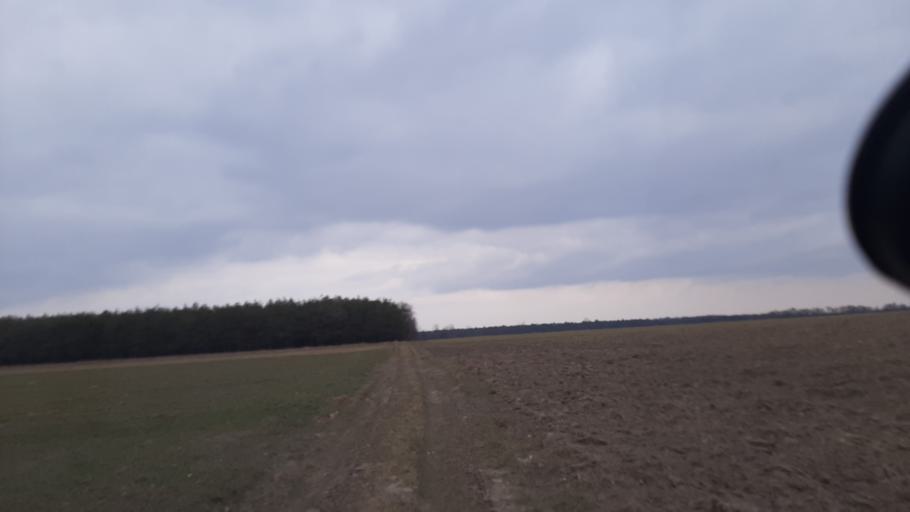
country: PL
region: Lublin Voivodeship
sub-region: Powiat lubelski
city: Garbow
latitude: 51.3836
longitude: 22.4080
